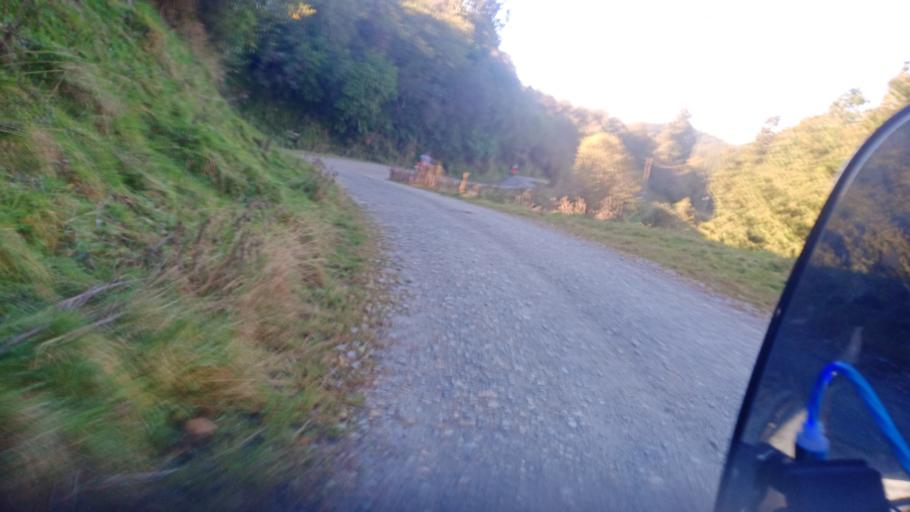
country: NZ
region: Hawke's Bay
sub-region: Wairoa District
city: Wairoa
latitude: -38.6650
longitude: 177.4805
